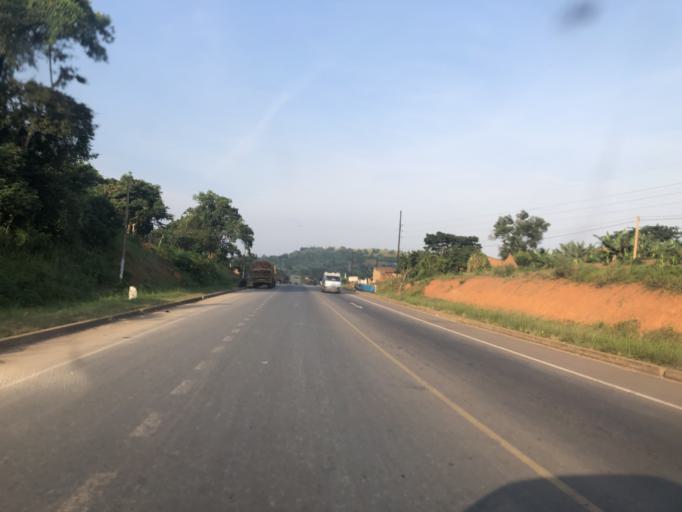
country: UG
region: Central Region
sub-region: Mpigi District
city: Mpigi
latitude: 0.1718
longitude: 32.2625
